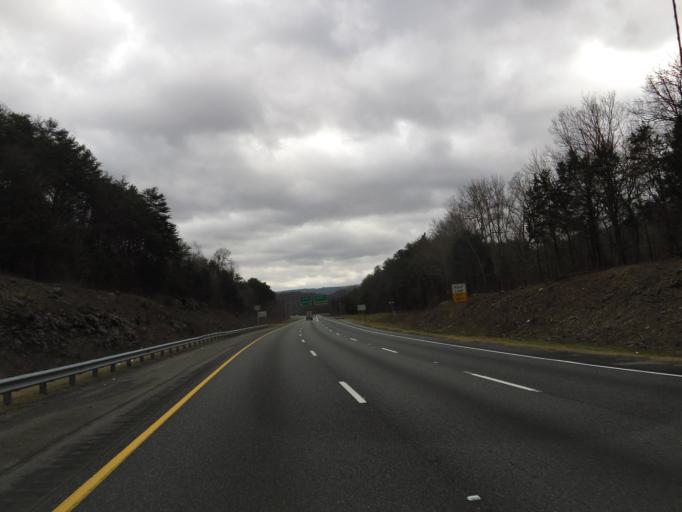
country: US
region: Georgia
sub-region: Walker County
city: Lookout Mountain
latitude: 34.9783
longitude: -85.4578
